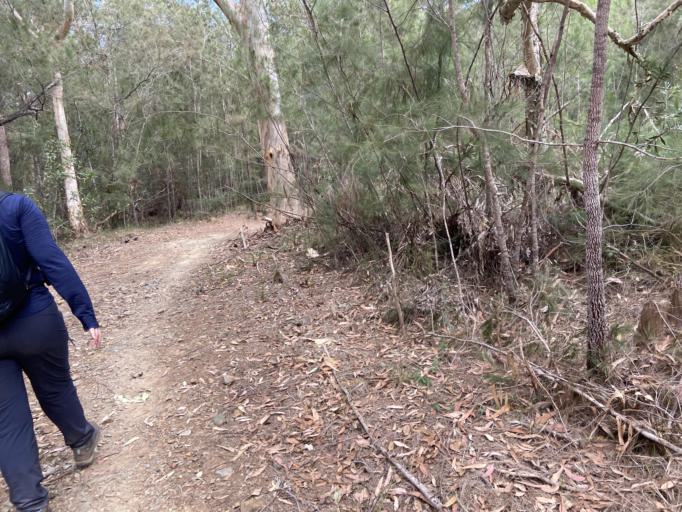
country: AU
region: Queensland
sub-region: Moreton Bay
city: Caboolture
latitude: -26.9498
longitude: 152.9560
